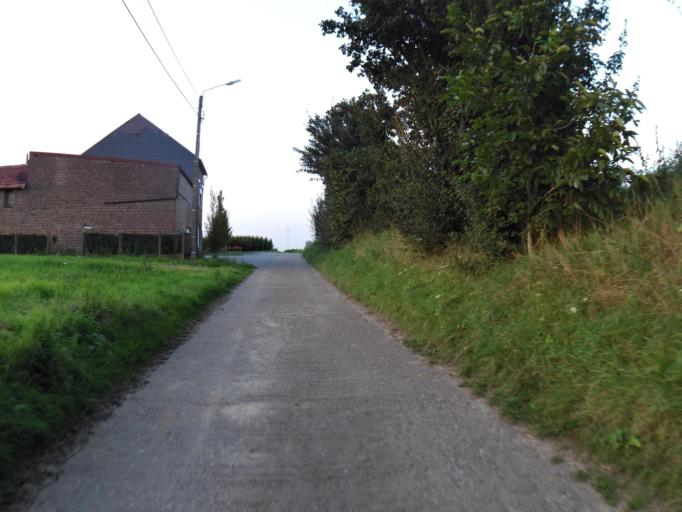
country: BE
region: Wallonia
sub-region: Province de Liege
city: Bassenge
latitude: 50.7702
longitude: 5.5600
